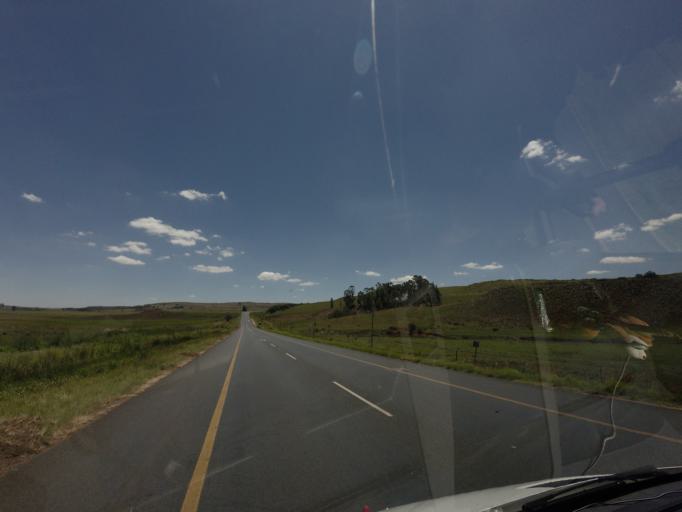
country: ZA
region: Mpumalanga
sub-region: Nkangala District Municipality
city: Belfast
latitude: -25.7115
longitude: 30.1774
